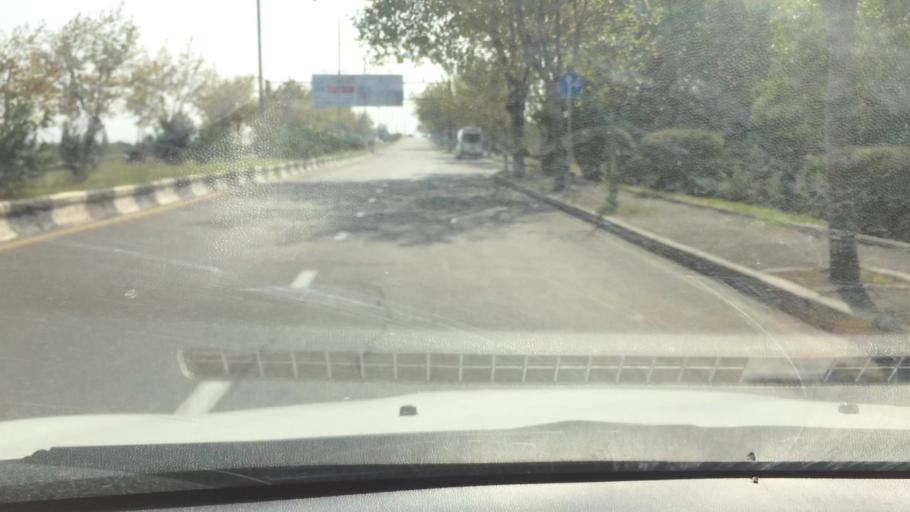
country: GE
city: Didi Lilo
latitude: 41.6897
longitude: 44.9528
